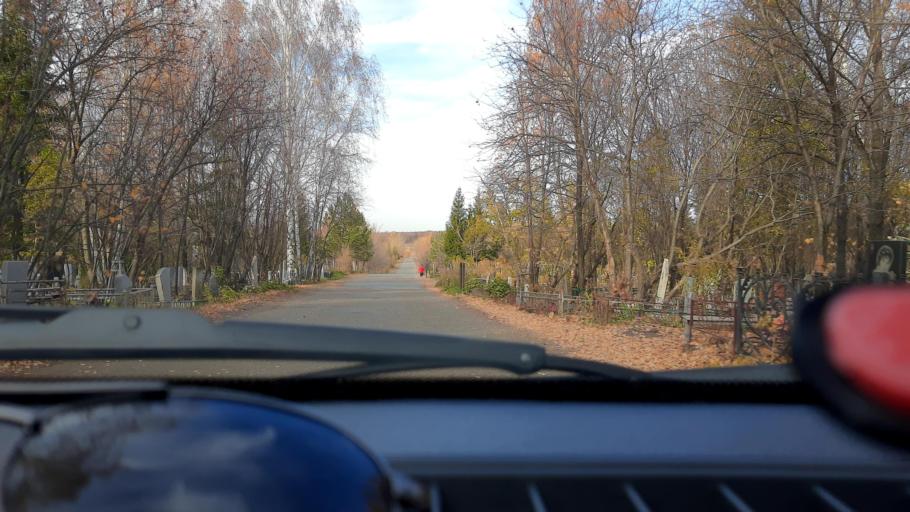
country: RU
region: Bashkortostan
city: Ufa
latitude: 54.8541
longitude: 56.1561
